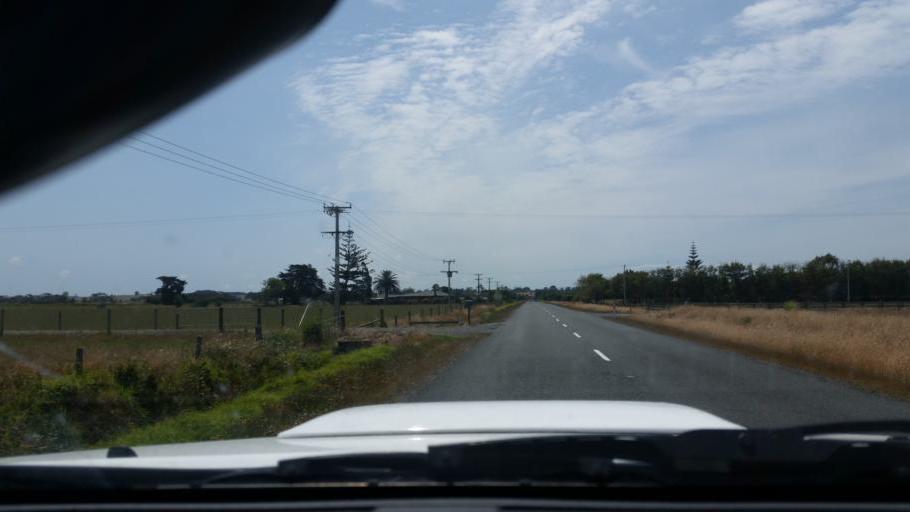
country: NZ
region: Northland
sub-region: Kaipara District
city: Dargaville
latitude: -36.0534
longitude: 173.9311
